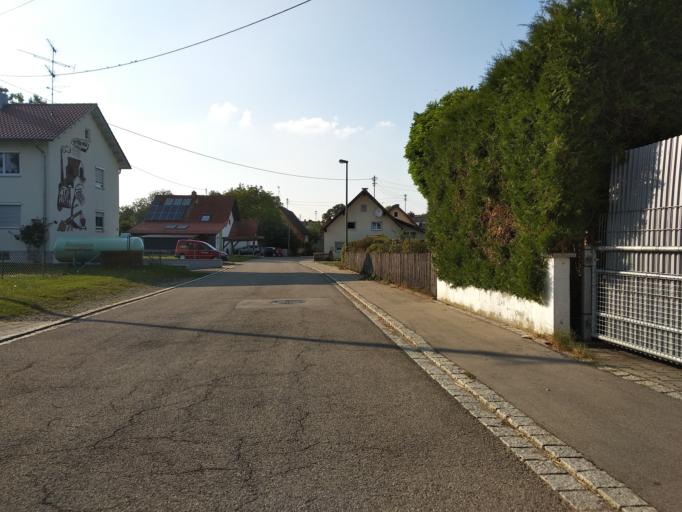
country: DE
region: Bavaria
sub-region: Swabia
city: Kronburg
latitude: 47.8944
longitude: 10.1455
